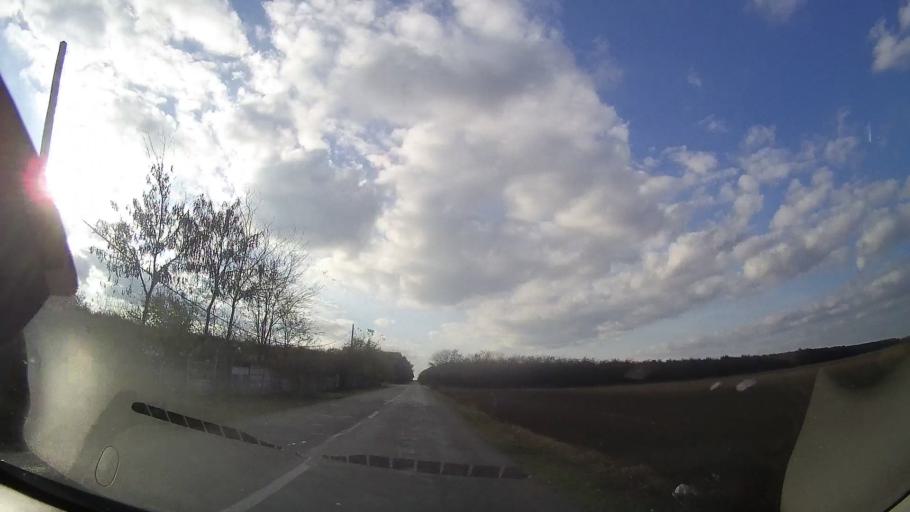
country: RO
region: Constanta
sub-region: Comuna Negru Voda
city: Negru Voda
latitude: 43.8193
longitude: 28.2858
